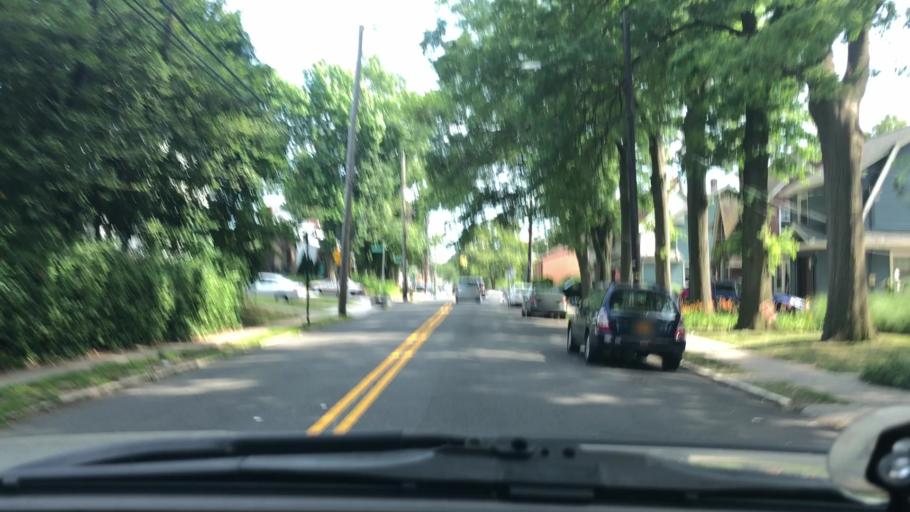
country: US
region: New Jersey
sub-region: Hudson County
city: Bayonne
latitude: 40.6242
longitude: -74.1138
